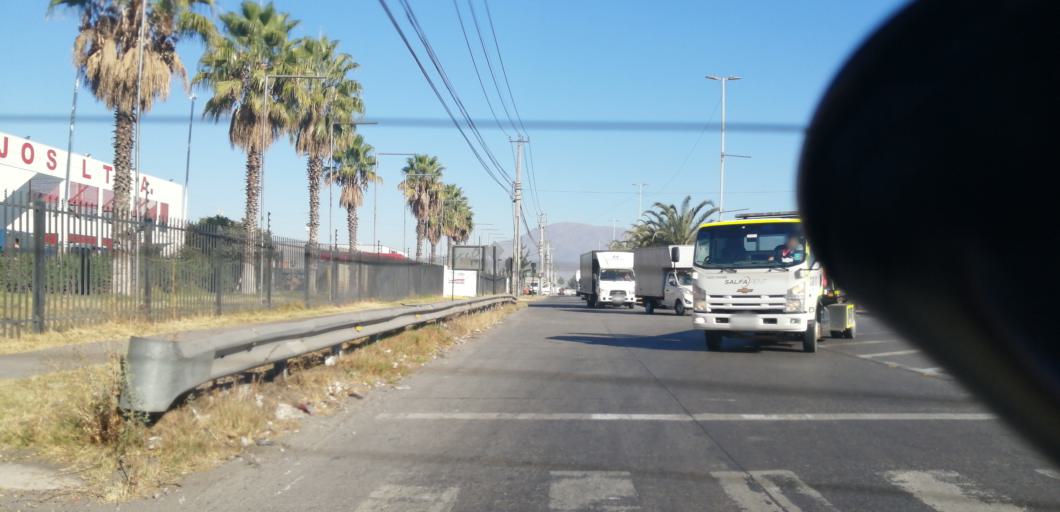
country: CL
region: Santiago Metropolitan
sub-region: Provincia de Santiago
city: Lo Prado
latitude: -33.4463
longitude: -70.7806
